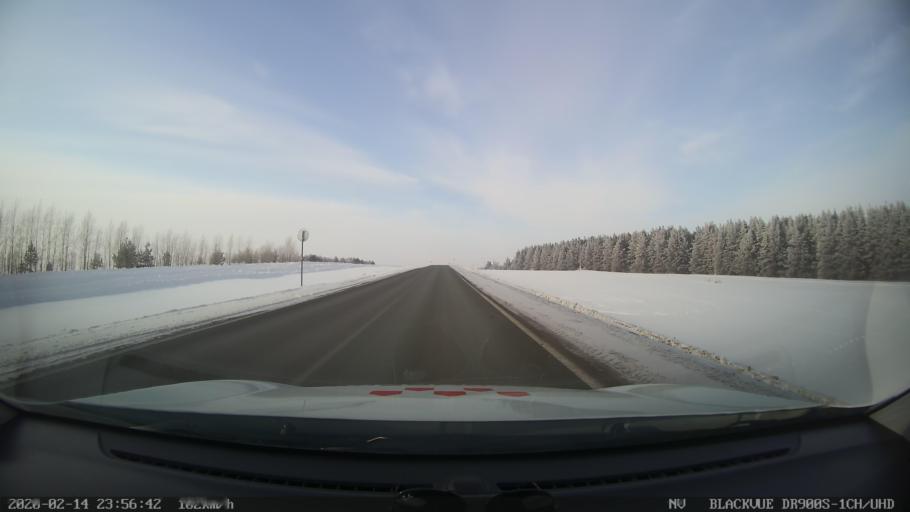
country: RU
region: Tatarstan
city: Kuybyshevskiy Zaton
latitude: 55.3279
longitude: 49.1250
